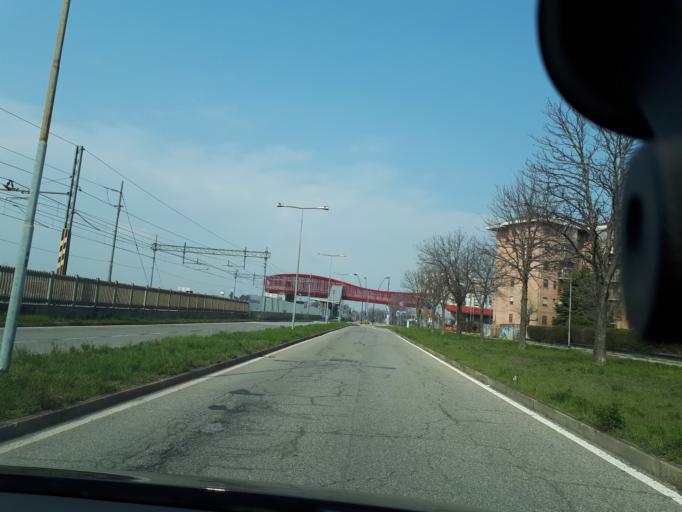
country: IT
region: Piedmont
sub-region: Provincia di Torino
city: Grugliasco
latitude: 45.0674
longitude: 7.6014
